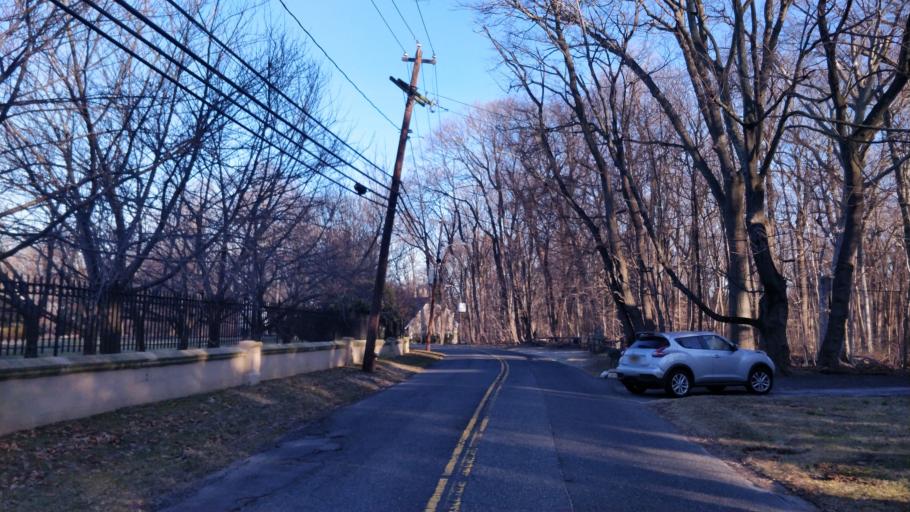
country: US
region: New York
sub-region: Nassau County
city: Glen Cove
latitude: 40.8718
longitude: -73.6473
